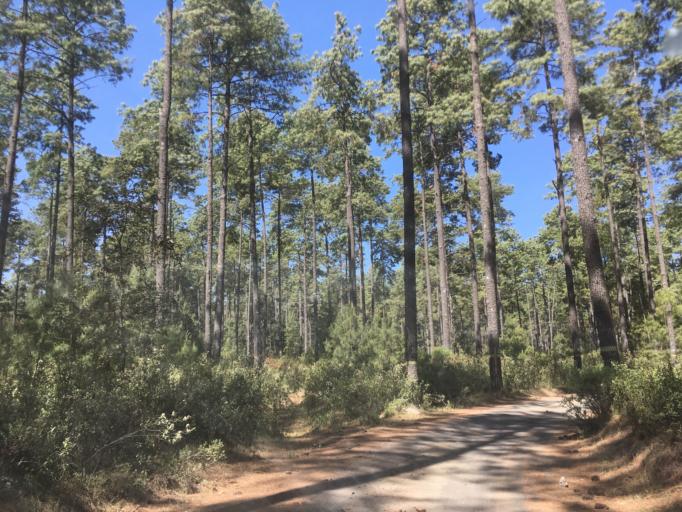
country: MX
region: Michoacan
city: Nuevo San Juan Parangaricutiro
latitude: 19.4598
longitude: -102.2086
